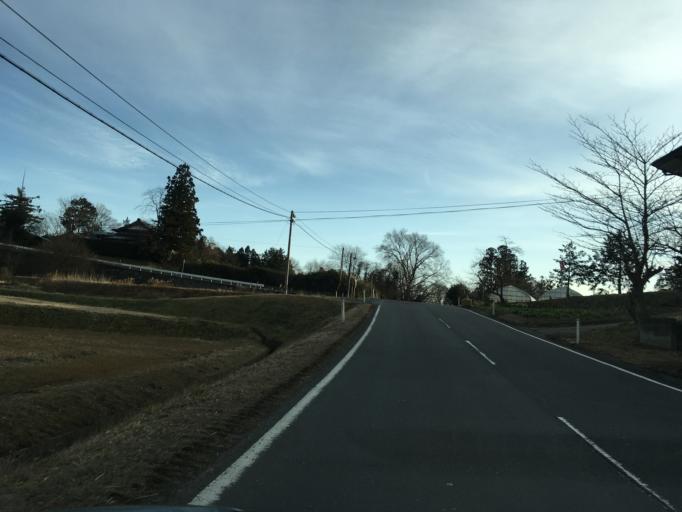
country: JP
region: Iwate
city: Ichinoseki
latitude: 38.7558
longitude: 141.1662
